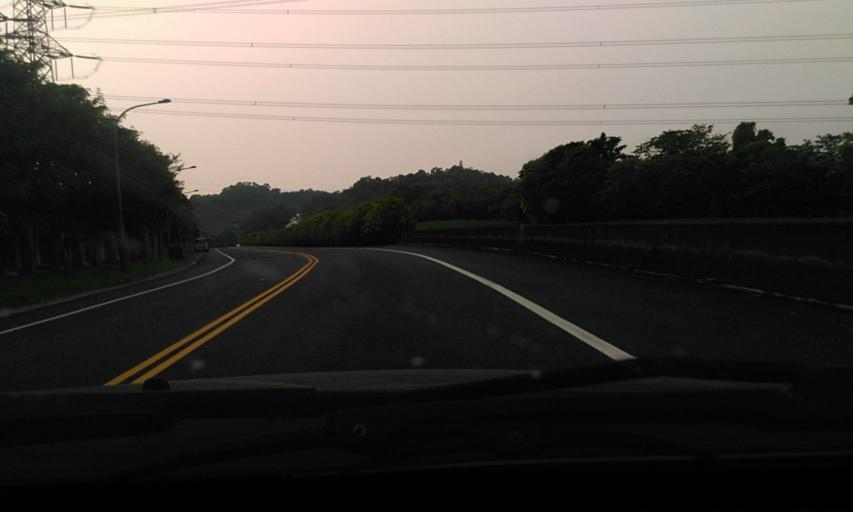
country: TW
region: Taiwan
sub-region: Hsinchu
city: Hsinchu
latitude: 24.6936
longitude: 120.9876
